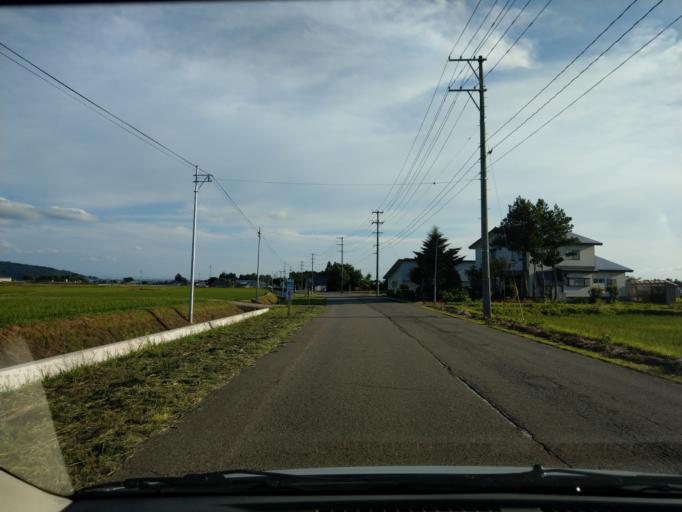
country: JP
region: Akita
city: Omagari
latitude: 39.4803
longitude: 140.5886
